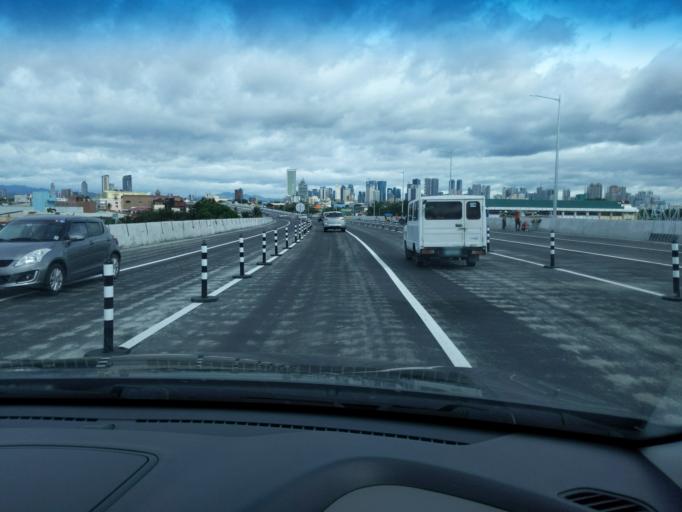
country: PH
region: Metro Manila
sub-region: San Juan
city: San Juan
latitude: 14.5887
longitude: 121.0164
